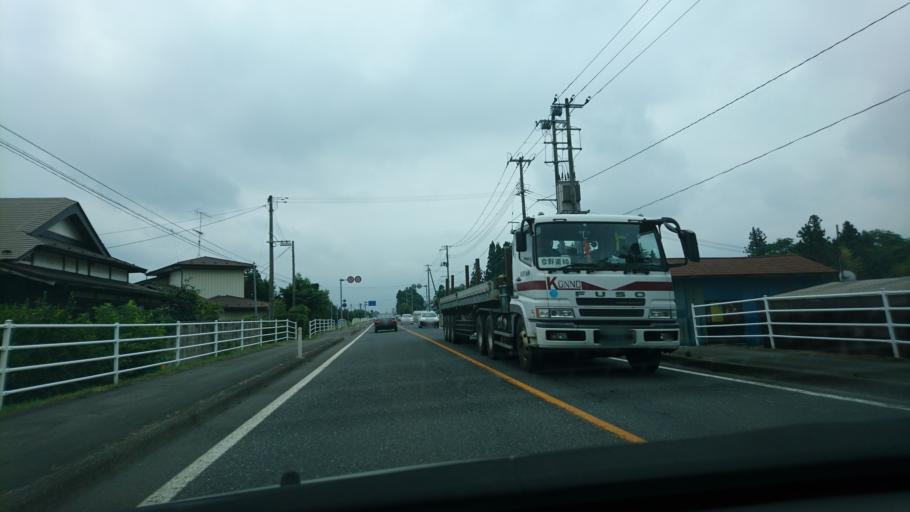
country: JP
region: Miyagi
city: Furukawa
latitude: 38.6998
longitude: 140.8410
